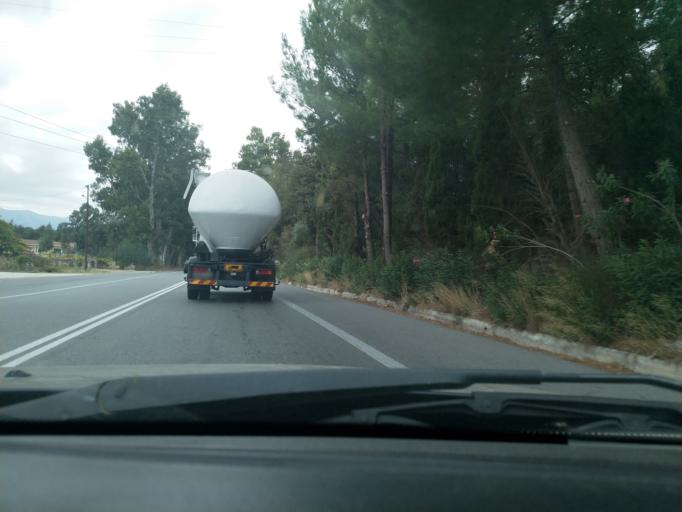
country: GR
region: Crete
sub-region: Nomos Chanias
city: Georgioupolis
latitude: 35.3790
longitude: 24.2041
